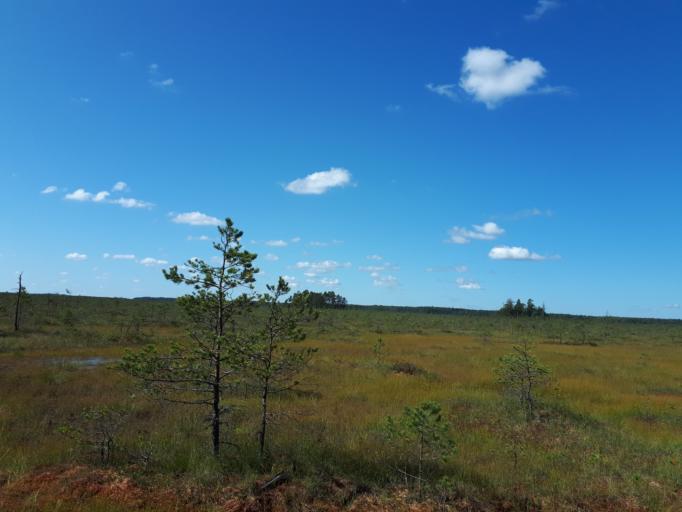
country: BY
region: Vitebsk
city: Rasony
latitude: 56.0562
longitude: 28.6219
